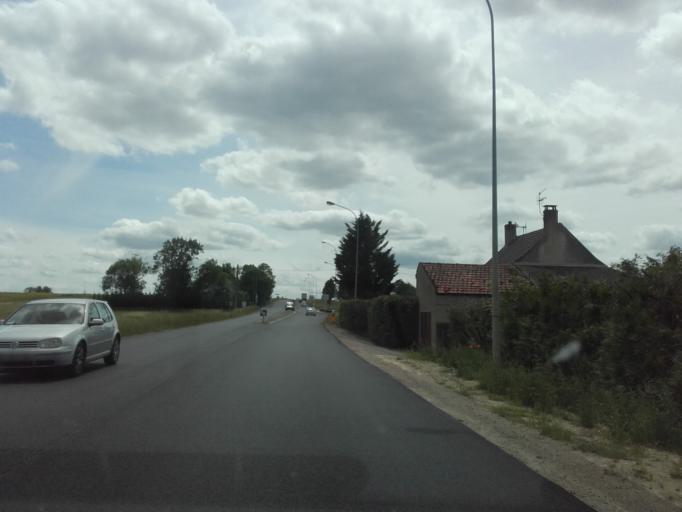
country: FR
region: Bourgogne
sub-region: Departement de la Cote-d'Or
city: Corpeau
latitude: 46.9435
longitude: 4.7607
